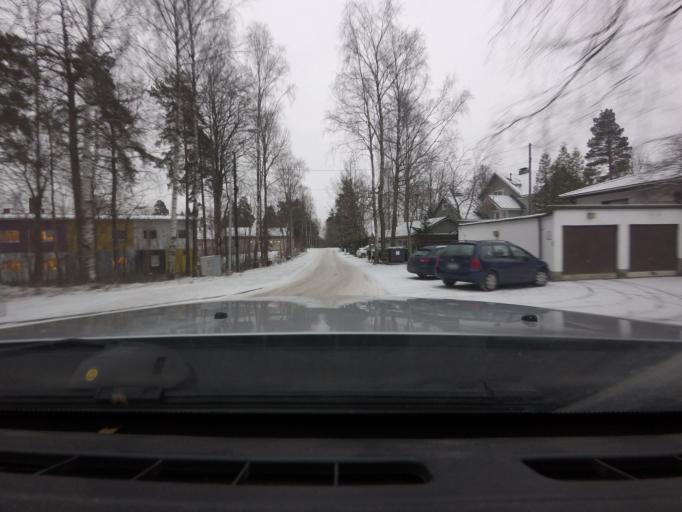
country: FI
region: Uusimaa
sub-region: Helsinki
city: Kauniainen
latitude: 60.2286
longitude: 24.7368
